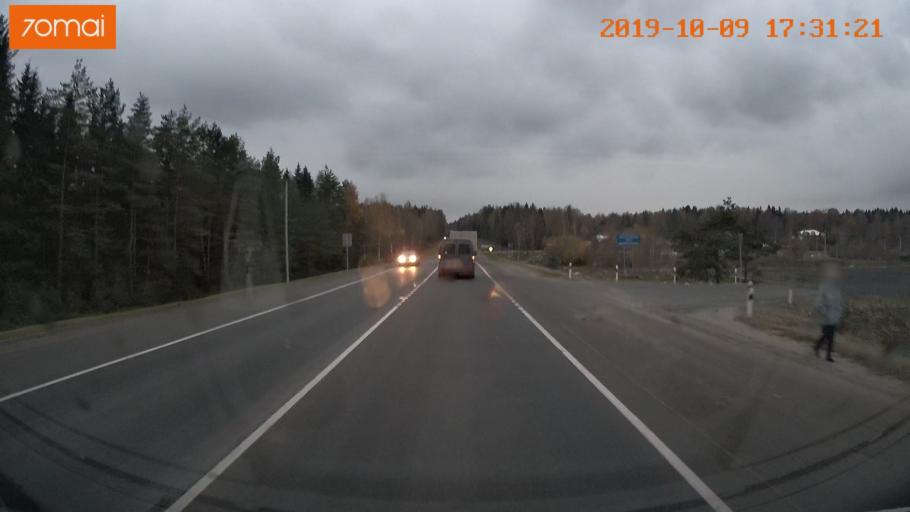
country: RU
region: Ivanovo
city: Bogorodskoye
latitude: 57.1361
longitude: 41.0401
